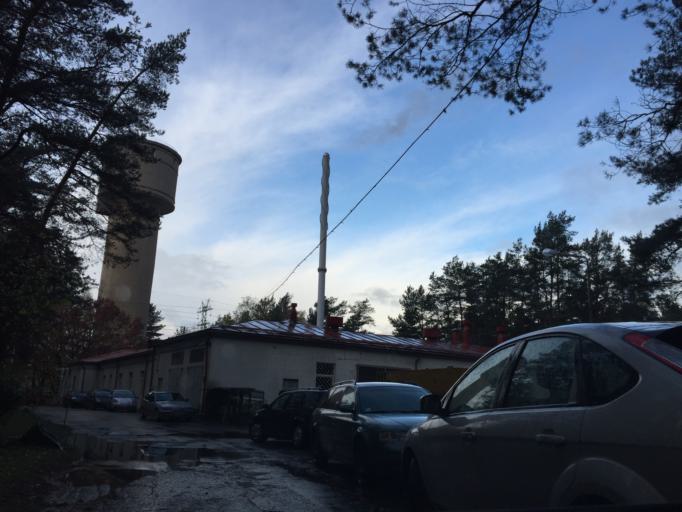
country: LV
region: Riga
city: Jaunciems
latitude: 56.9693
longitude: 24.1976
